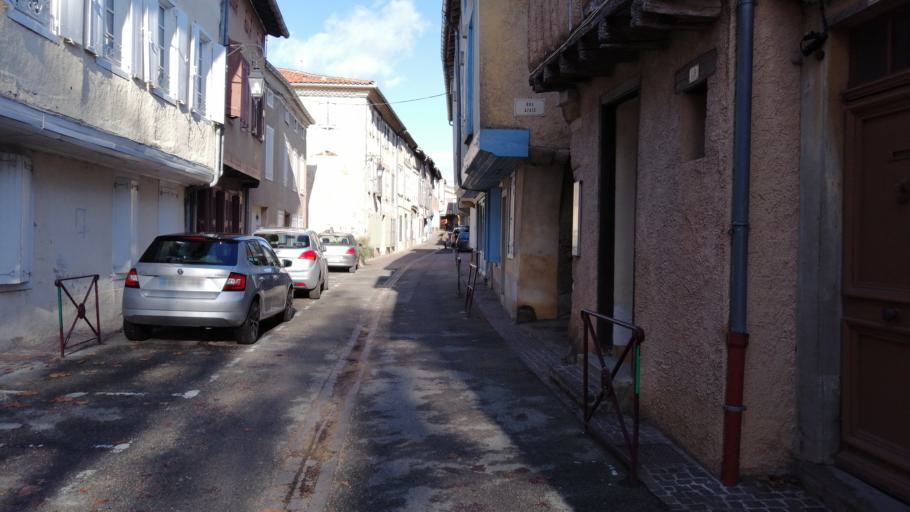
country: FR
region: Midi-Pyrenees
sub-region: Departement du Tarn
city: Soreze
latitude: 43.4517
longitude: 2.0655
